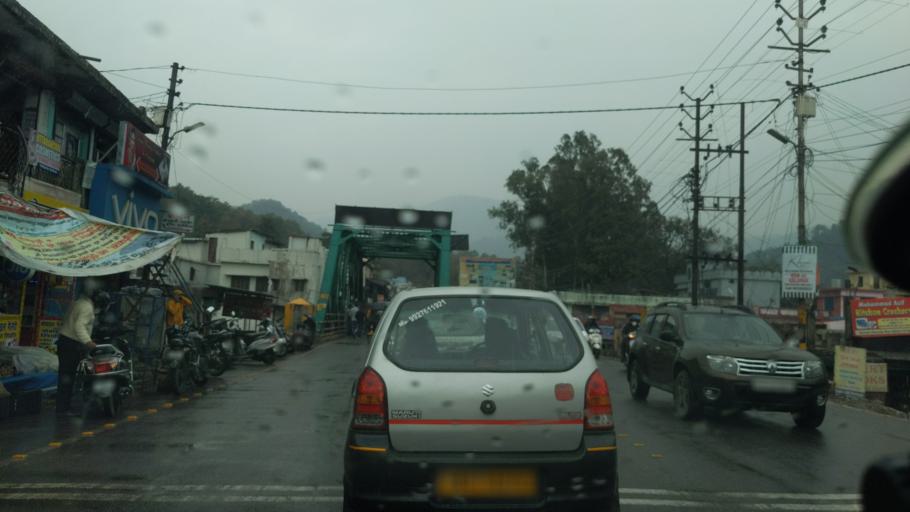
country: IN
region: Uttarakhand
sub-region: Naini Tal
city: Haldwani
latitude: 29.2704
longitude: 79.5440
